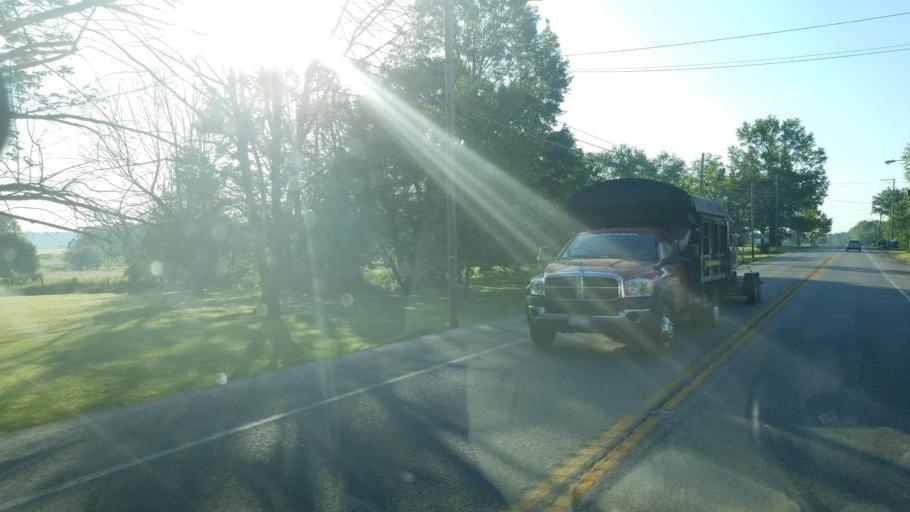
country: US
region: Ohio
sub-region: Wayne County
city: Apple Creek
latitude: 40.7627
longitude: -81.8934
